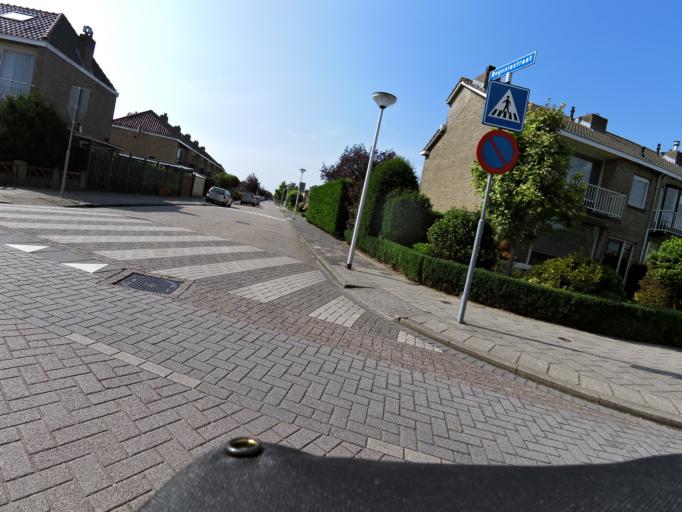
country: NL
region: South Holland
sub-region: Gemeente Oud-Beijerland
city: Oud-Beijerland
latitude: 51.8208
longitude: 4.4221
